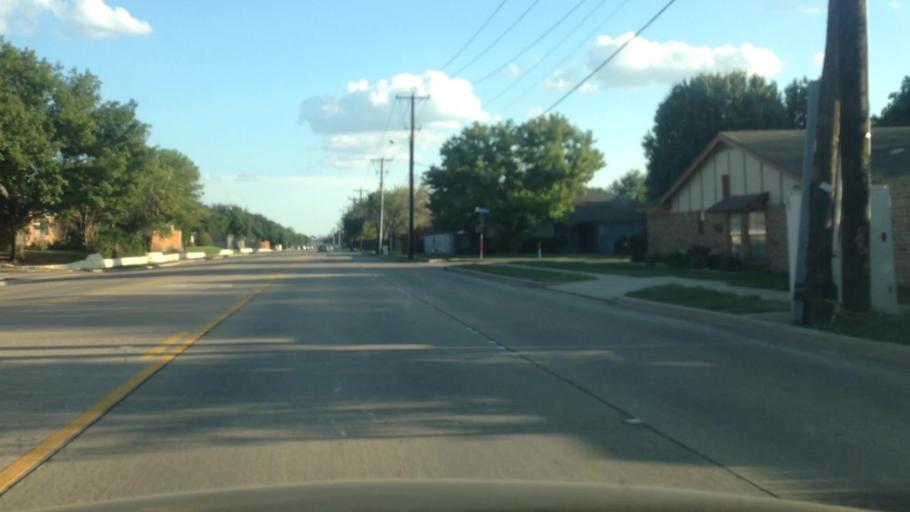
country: US
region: Texas
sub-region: Tarrant County
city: Watauga
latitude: 32.8860
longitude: -97.2378
